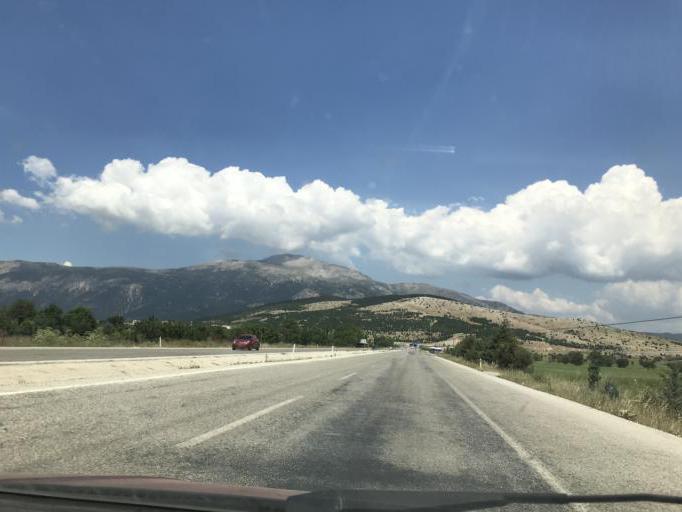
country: TR
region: Denizli
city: Serinhisar
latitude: 37.6245
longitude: 29.2037
